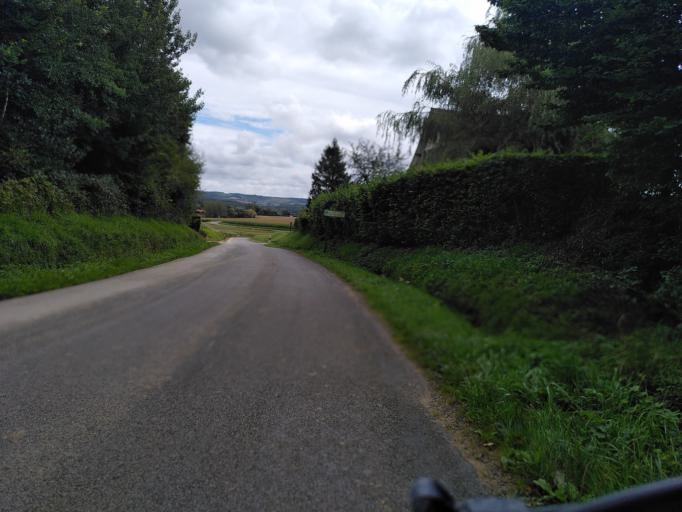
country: FR
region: Nord-Pas-de-Calais
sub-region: Departement du Pas-de-Calais
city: Longfosse
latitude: 50.7021
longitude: 1.7693
